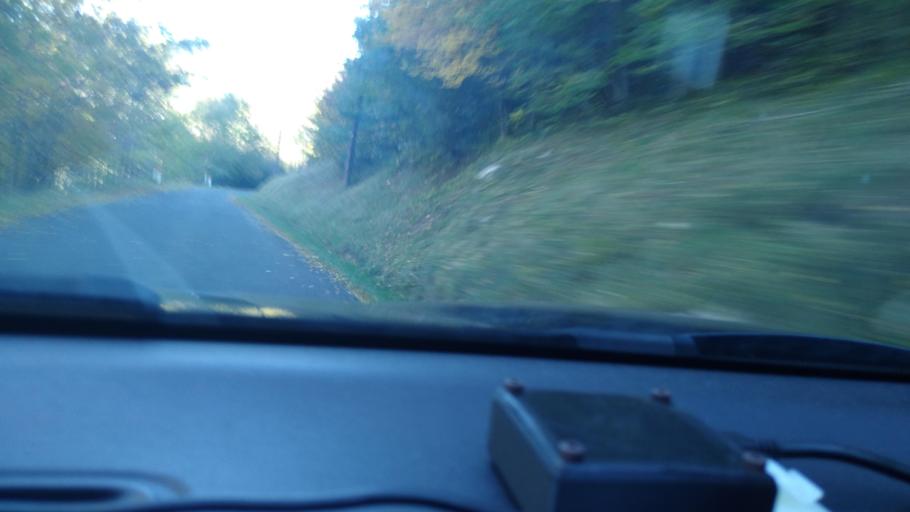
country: FR
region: Languedoc-Roussillon
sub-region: Departement de l'Aude
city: Quillan
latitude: 42.7337
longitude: 2.1201
